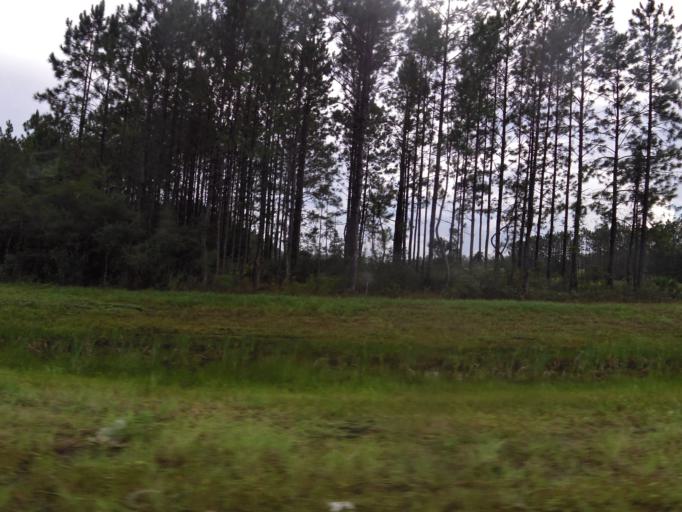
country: US
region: Florida
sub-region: Duval County
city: Baldwin
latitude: 30.3065
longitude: -81.8766
